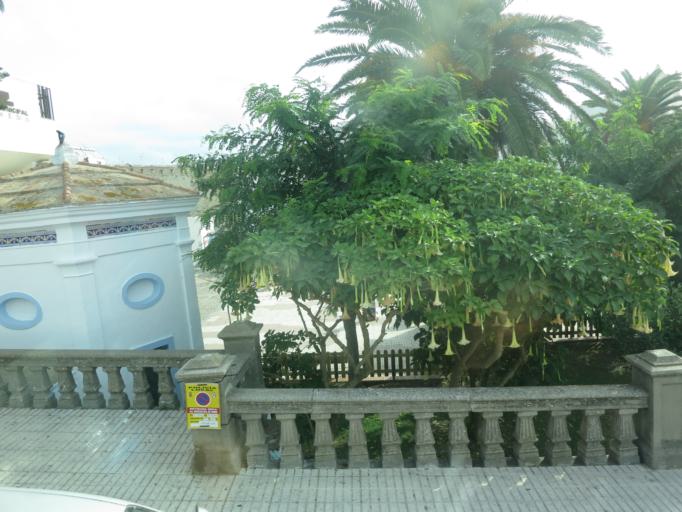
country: ES
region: Andalusia
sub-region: Provincia de Cadiz
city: Tarifa
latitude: 36.0128
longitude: -5.6052
